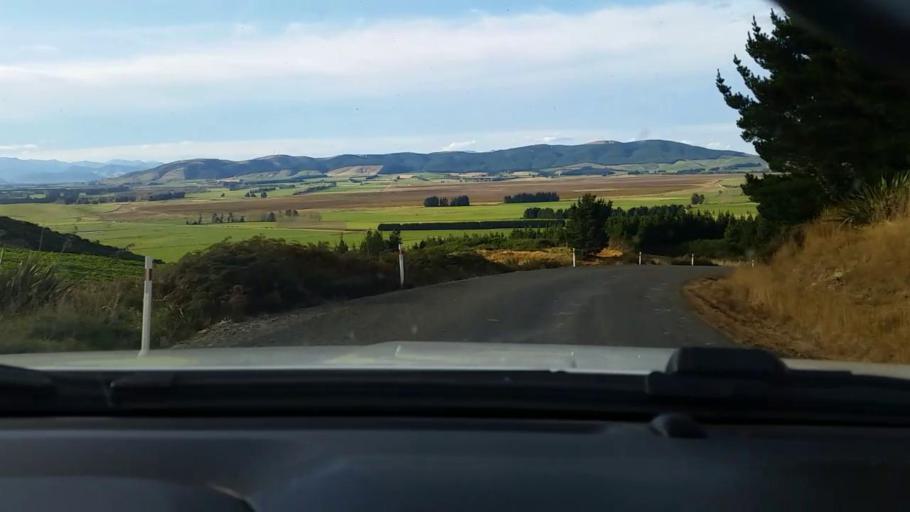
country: NZ
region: Southland
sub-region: Southland District
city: Winton
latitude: -45.8189
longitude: 168.1746
